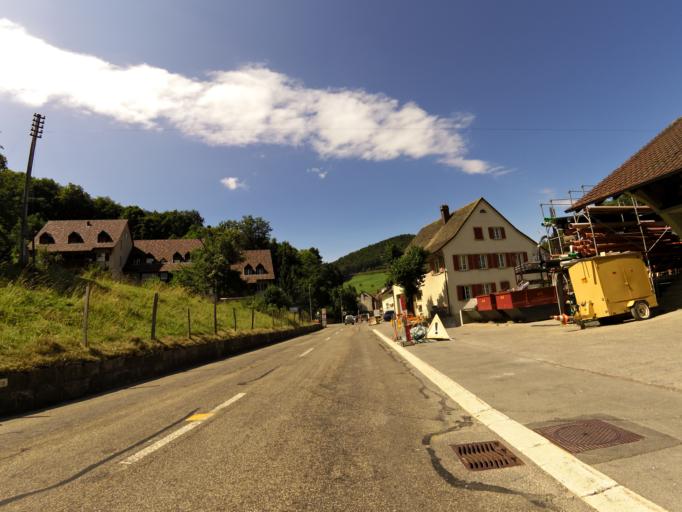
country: CH
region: Basel-Landschaft
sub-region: Bezirk Waldenburg
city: Langenbruck
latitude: 47.3462
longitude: 7.7695
